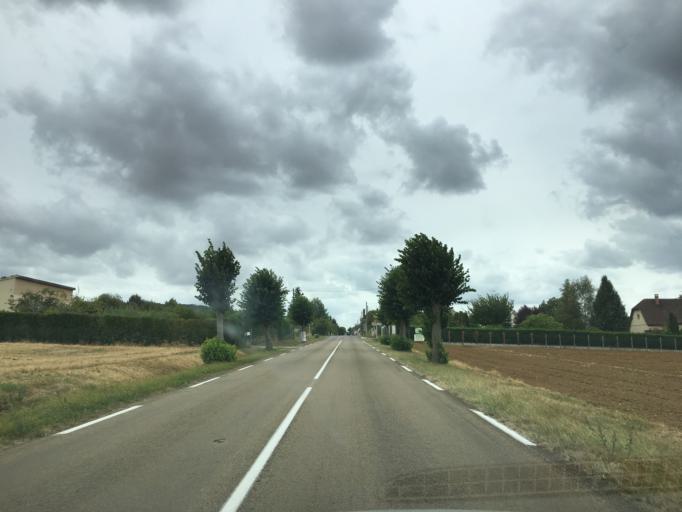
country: FR
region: Bourgogne
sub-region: Departement de l'Yonne
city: Joigny
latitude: 47.9582
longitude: 3.3786
